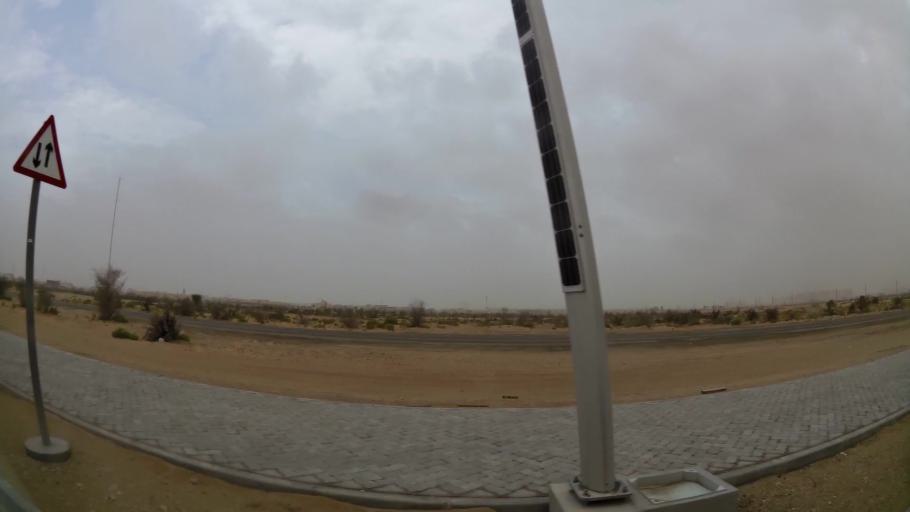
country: AE
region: Abu Dhabi
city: Abu Dhabi
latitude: 24.4206
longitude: 54.6146
